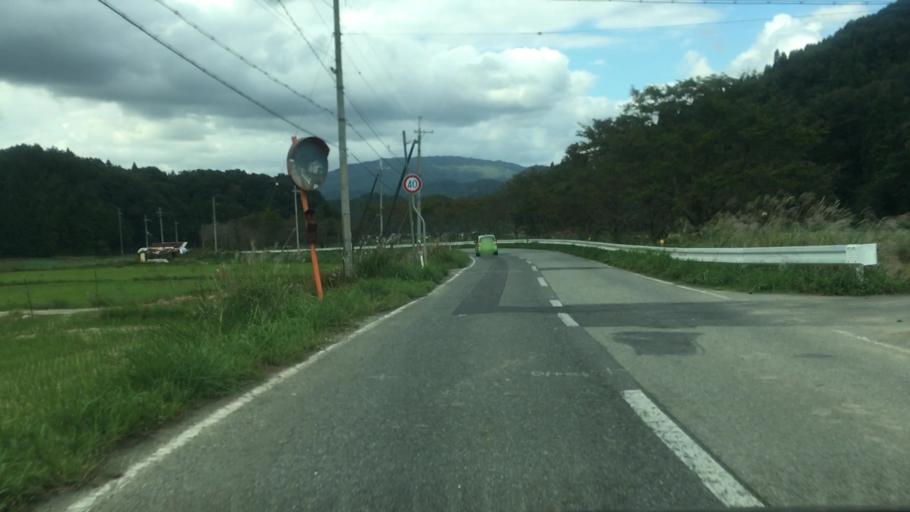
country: JP
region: Hyogo
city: Toyooka
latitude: 35.4415
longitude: 134.7316
